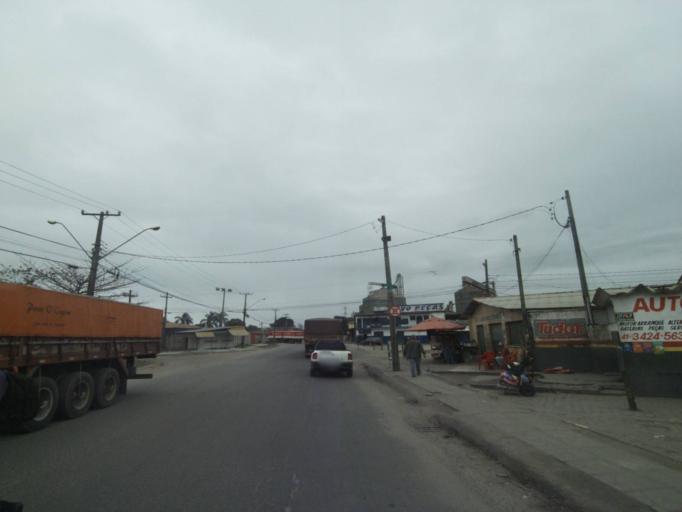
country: BR
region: Parana
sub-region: Paranagua
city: Paranagua
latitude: -25.5509
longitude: -48.5529
